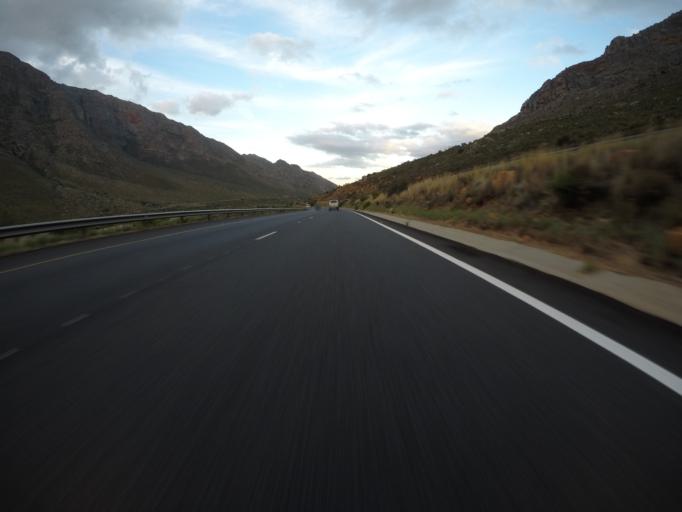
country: ZA
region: Western Cape
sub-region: Cape Winelands District Municipality
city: Paarl
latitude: -33.6995
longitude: 19.2118
